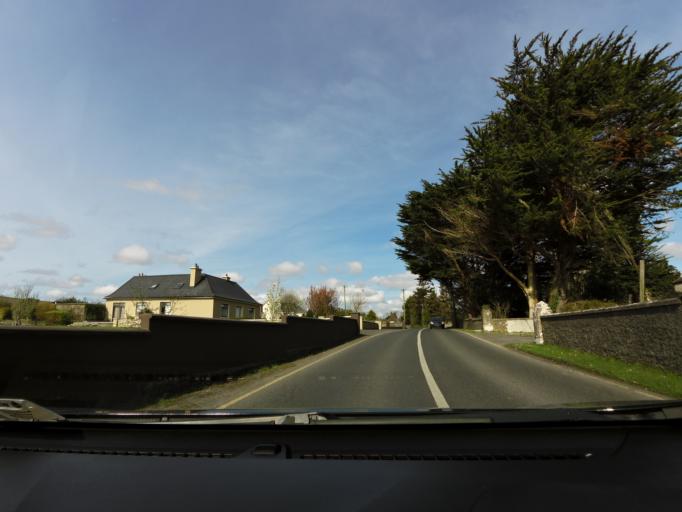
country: IE
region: Connaught
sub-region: County Galway
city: Claregalway
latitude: 53.3438
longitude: -8.8871
